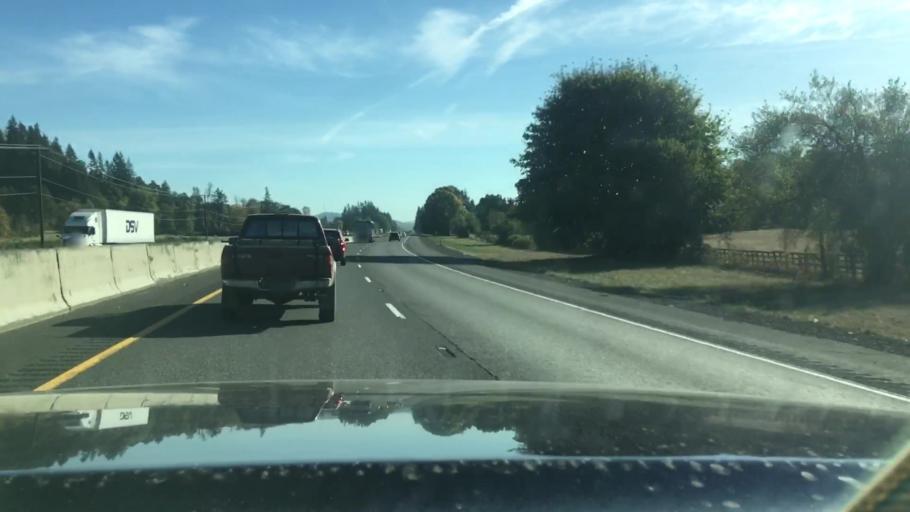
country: US
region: Oregon
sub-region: Lane County
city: Creswell
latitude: 43.8676
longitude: -123.0153
